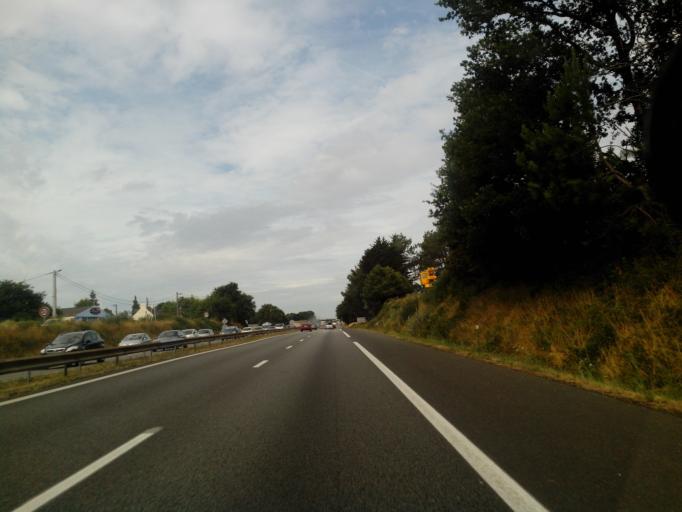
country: FR
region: Brittany
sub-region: Departement du Morbihan
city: Ploeren
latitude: 47.6610
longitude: -2.8503
